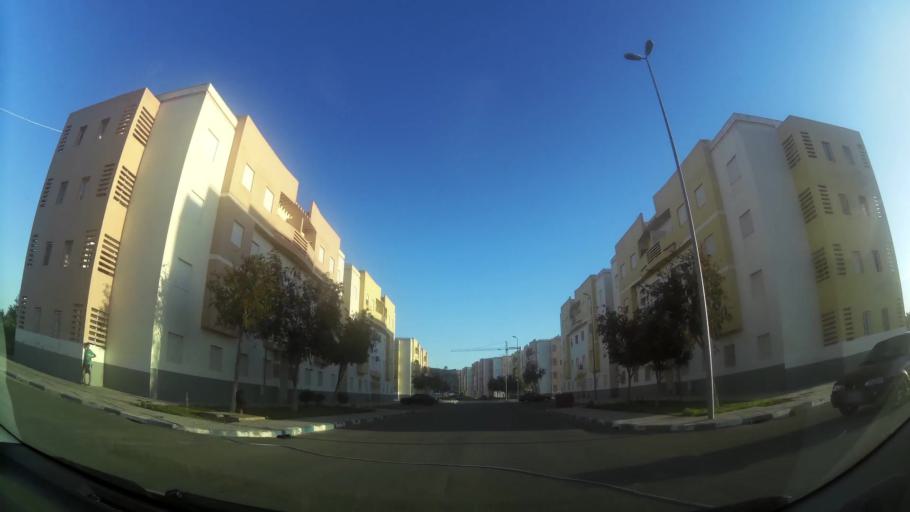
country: MA
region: Oriental
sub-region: Berkane-Taourirt
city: Madagh
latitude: 35.0783
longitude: -2.2372
